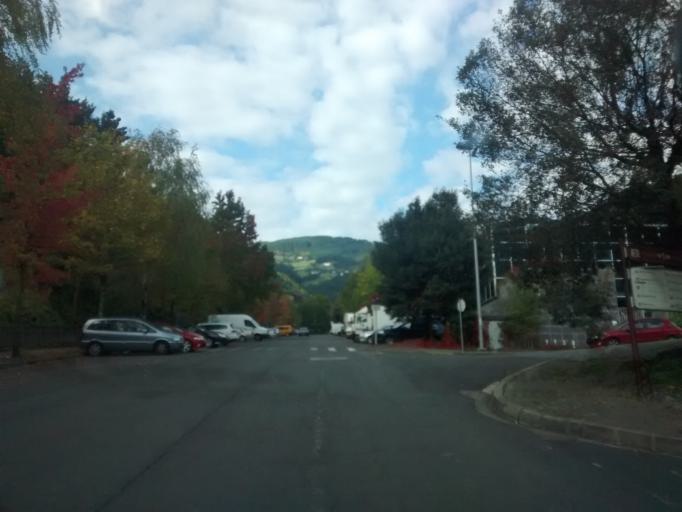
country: ES
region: Basque Country
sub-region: Provincia de Guipuzcoa
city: Eibar
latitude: 43.1923
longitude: -2.4528
